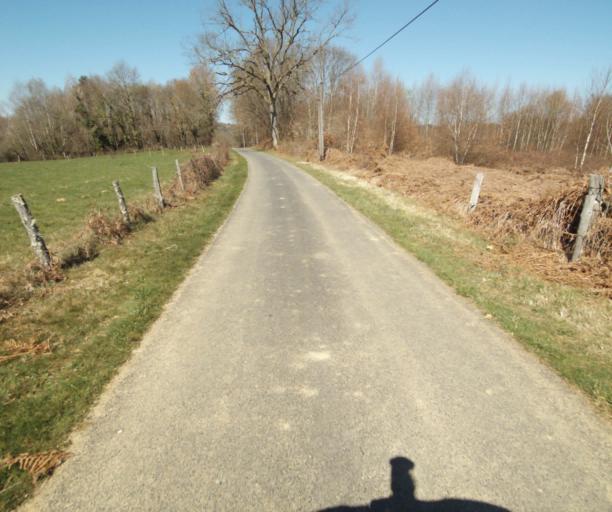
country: FR
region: Limousin
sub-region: Departement de la Correze
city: Saint-Clement
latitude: 45.3145
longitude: 1.6978
